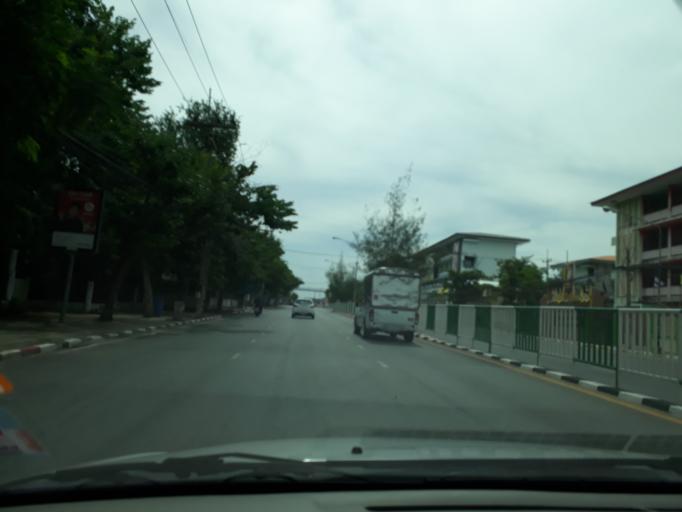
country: TH
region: Khon Kaen
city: Khon Kaen
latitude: 16.4382
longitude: 102.8381
